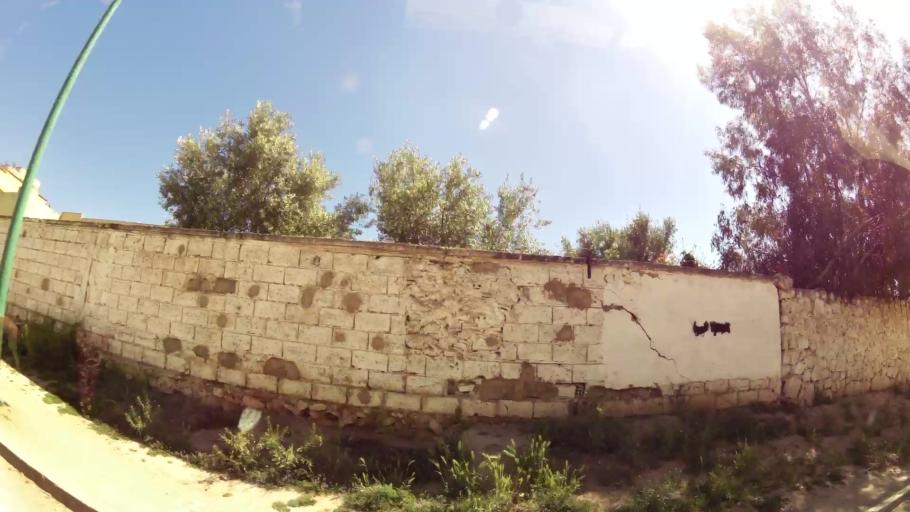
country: MA
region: Meknes-Tafilalet
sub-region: Meknes
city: Meknes
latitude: 33.8896
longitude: -5.5733
